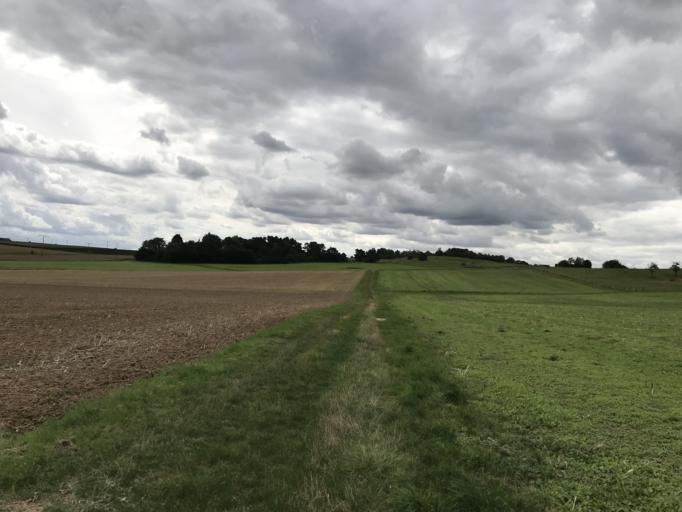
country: DE
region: Hesse
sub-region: Regierungsbezirk Giessen
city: Grunberg
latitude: 50.6262
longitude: 8.9771
